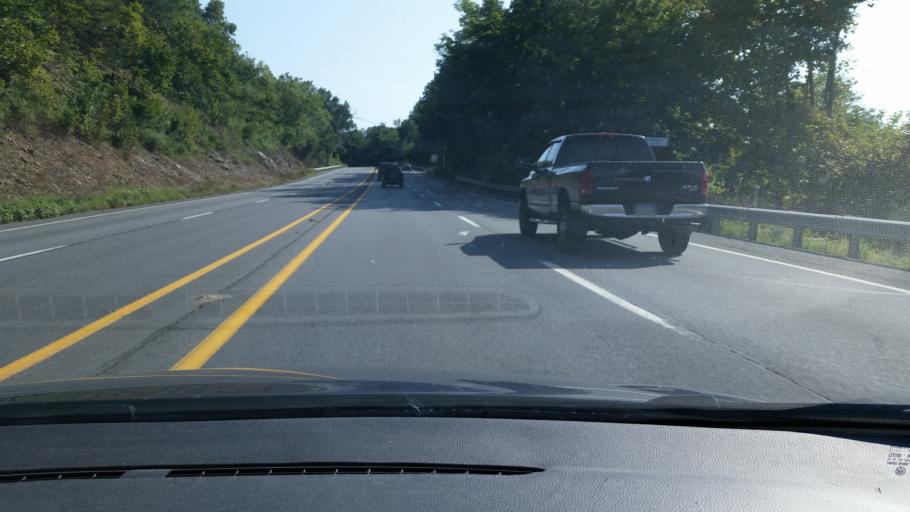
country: US
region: Pennsylvania
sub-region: Berks County
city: Hamburg
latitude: 40.5317
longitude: -75.9753
